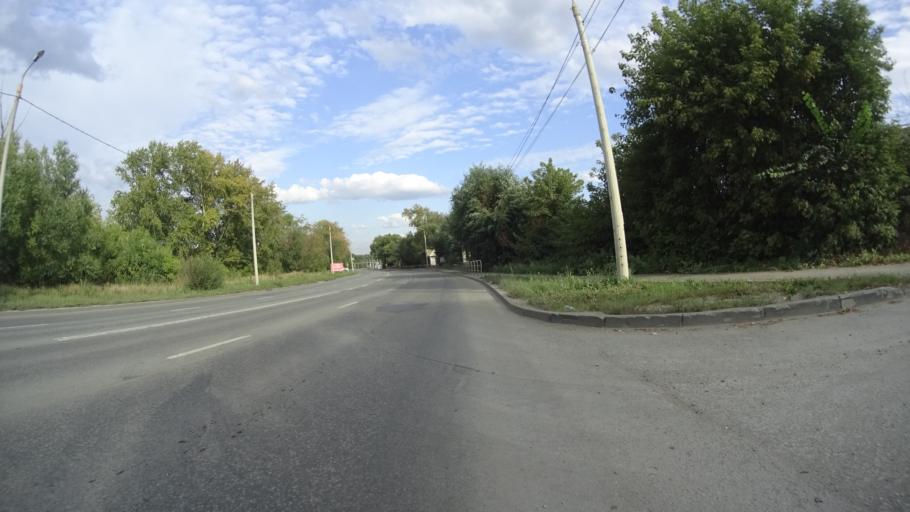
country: RU
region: Chelyabinsk
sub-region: Gorod Chelyabinsk
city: Chelyabinsk
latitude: 55.1962
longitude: 61.3757
